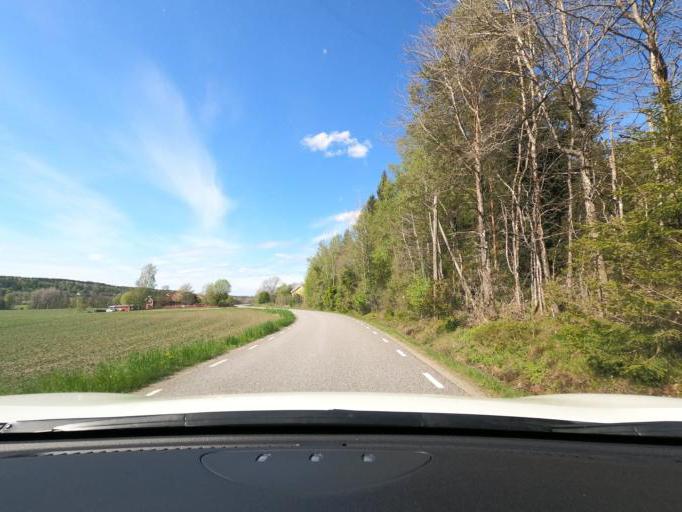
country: SE
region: Vaestra Goetaland
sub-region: Harryda Kommun
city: Ravlanda
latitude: 57.6163
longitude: 12.4958
